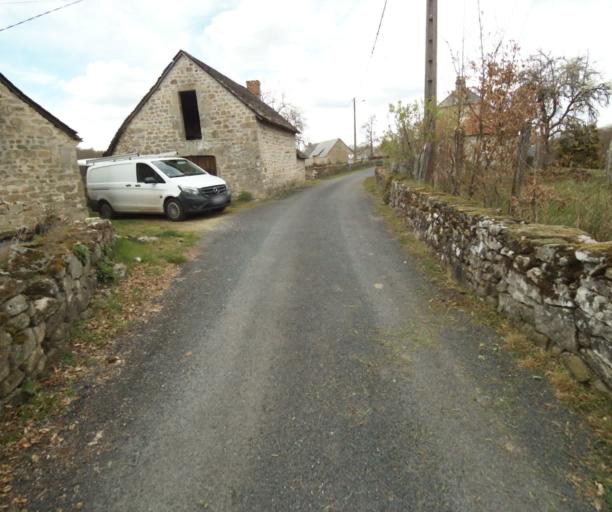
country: FR
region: Limousin
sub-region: Departement de la Correze
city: Argentat
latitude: 45.2120
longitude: 1.9194
